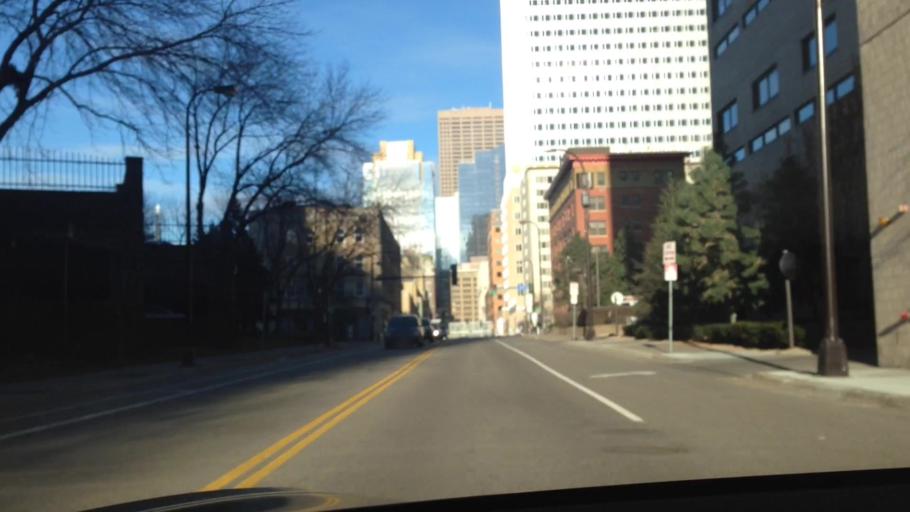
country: US
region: Minnesota
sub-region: Hennepin County
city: Minneapolis
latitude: 44.9719
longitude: -93.2785
